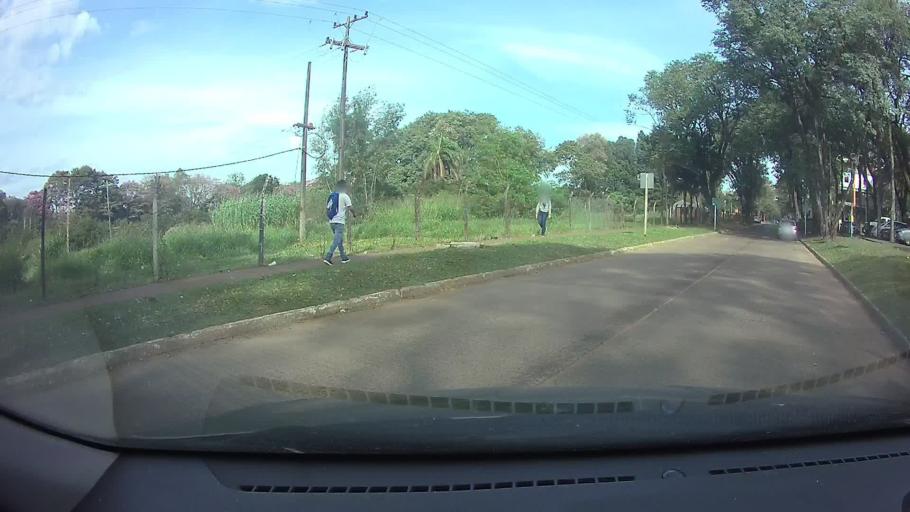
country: PY
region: Central
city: Fernando de la Mora
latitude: -25.3359
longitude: -57.5178
